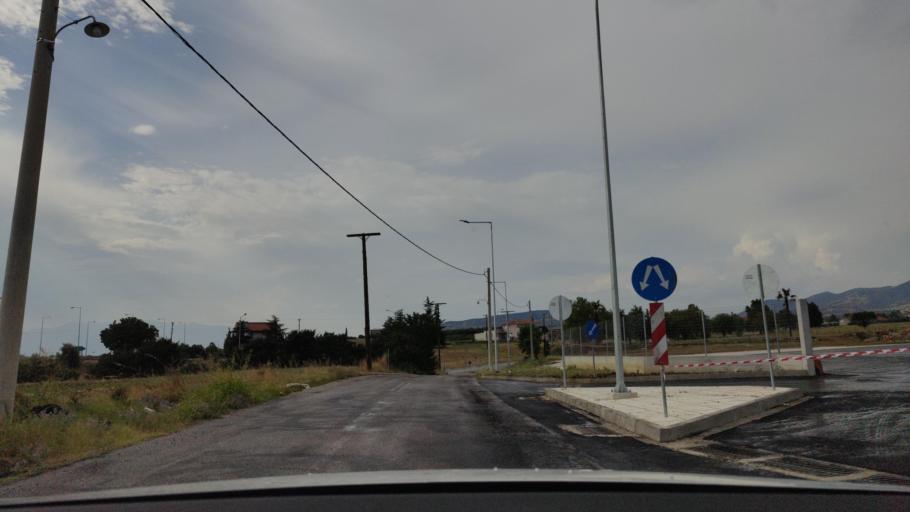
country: GR
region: Central Macedonia
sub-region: Nomos Serron
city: Kala Dendra
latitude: 41.1356
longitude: 23.4416
